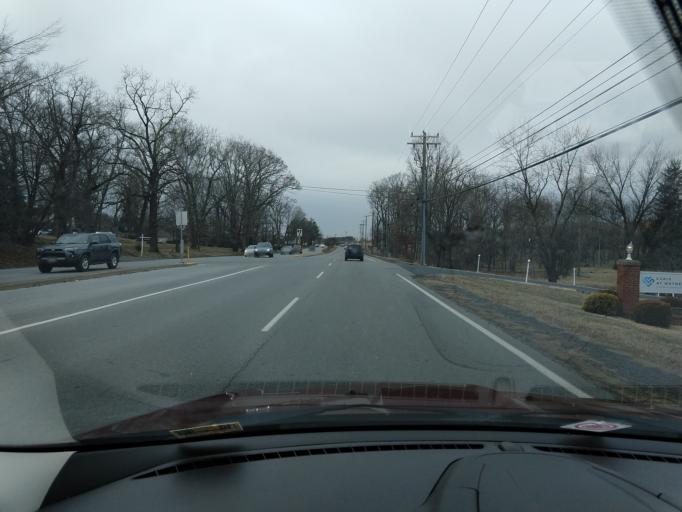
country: US
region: Virginia
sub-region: City of Waynesboro
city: Waynesboro
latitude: 38.0673
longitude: -78.9263
